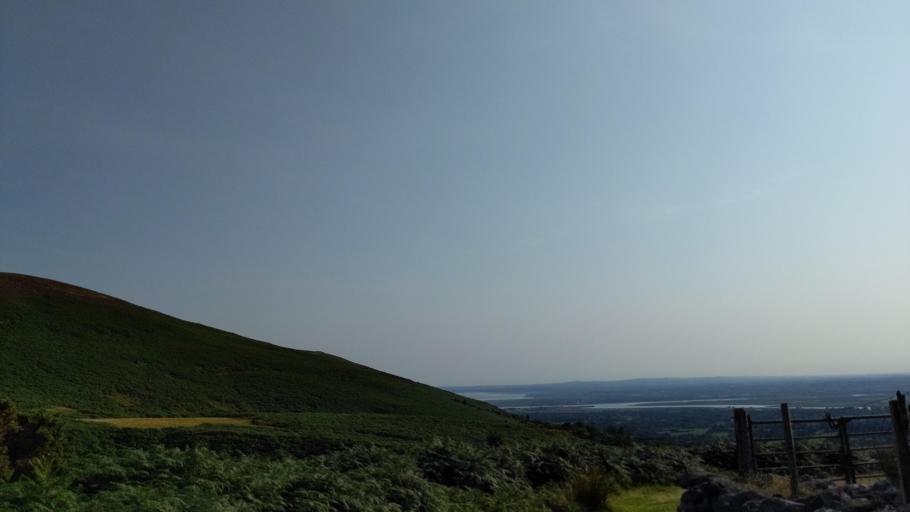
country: GB
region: Northern Ireland
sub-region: Down District
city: Warrenpoint
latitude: 54.0631
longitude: -6.3240
